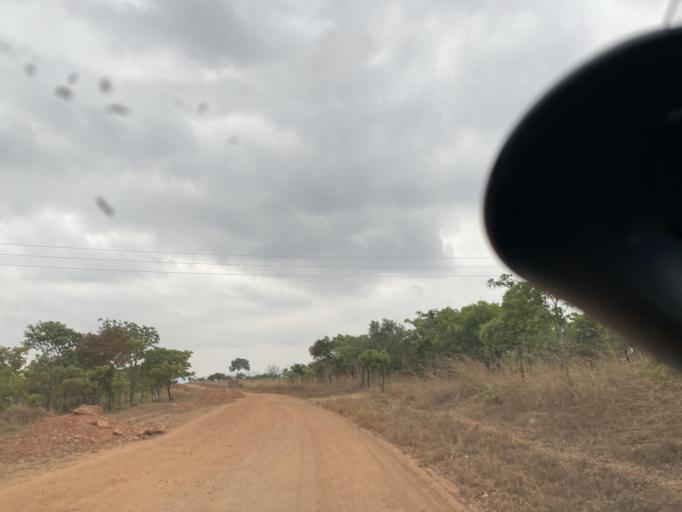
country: ZM
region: Lusaka
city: Chongwe
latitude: -15.2597
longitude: 28.7316
